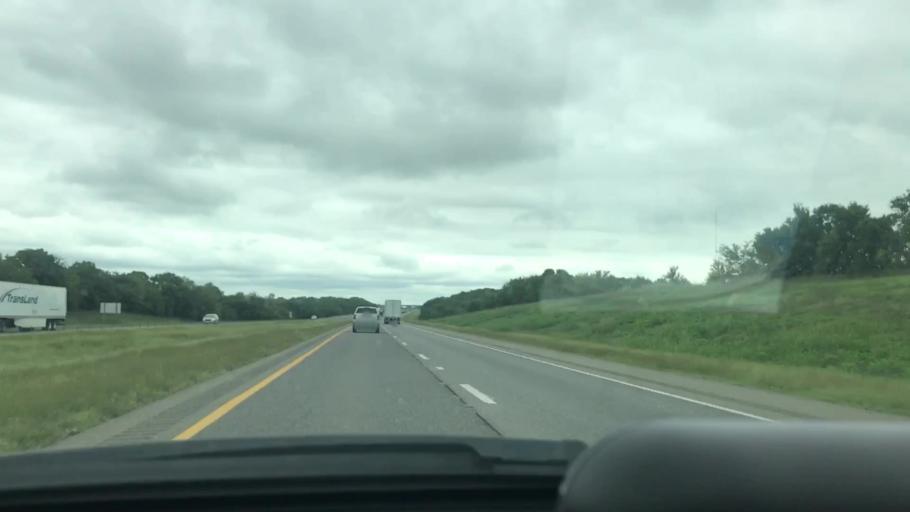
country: US
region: Oklahoma
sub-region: McIntosh County
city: Checotah
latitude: 35.3918
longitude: -95.5653
